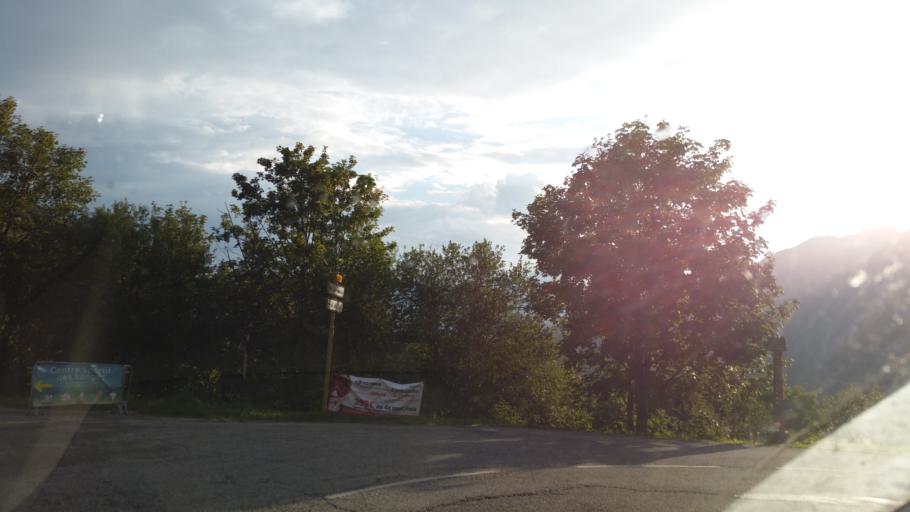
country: FR
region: Rhone-Alpes
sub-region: Departement de la Savoie
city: La Chambre
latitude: 45.4160
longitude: 6.3627
